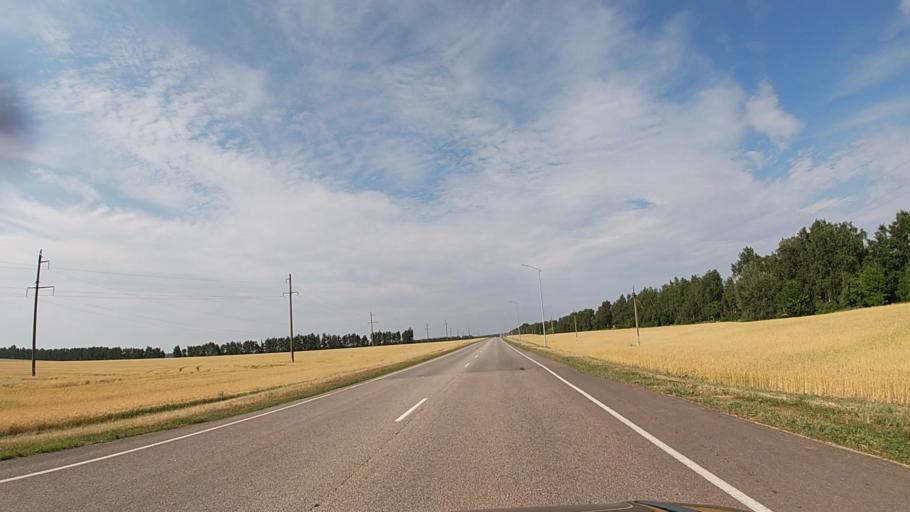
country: RU
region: Belgorod
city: Proletarskiy
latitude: 50.8251
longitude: 35.7600
